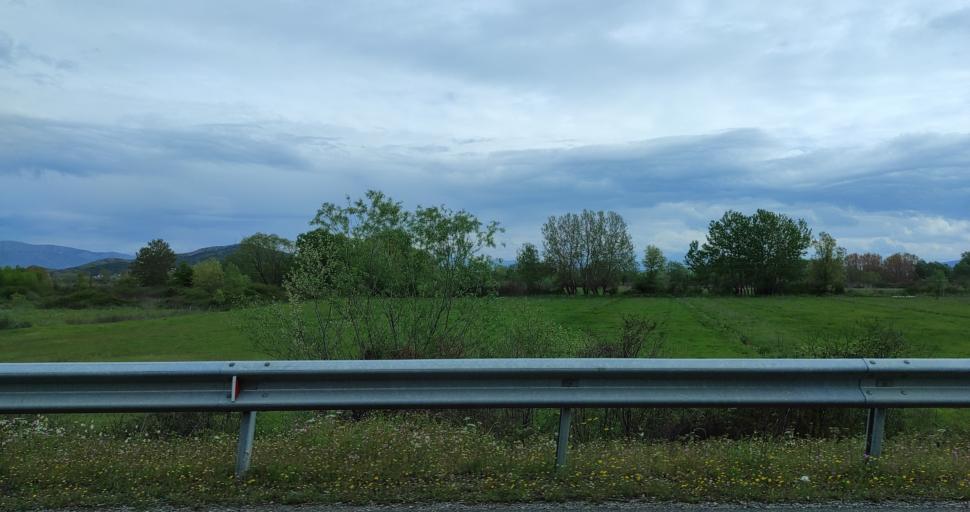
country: AL
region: Shkoder
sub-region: Rrethi i Shkodres
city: Berdica e Madhe
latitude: 42.0201
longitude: 19.4565
